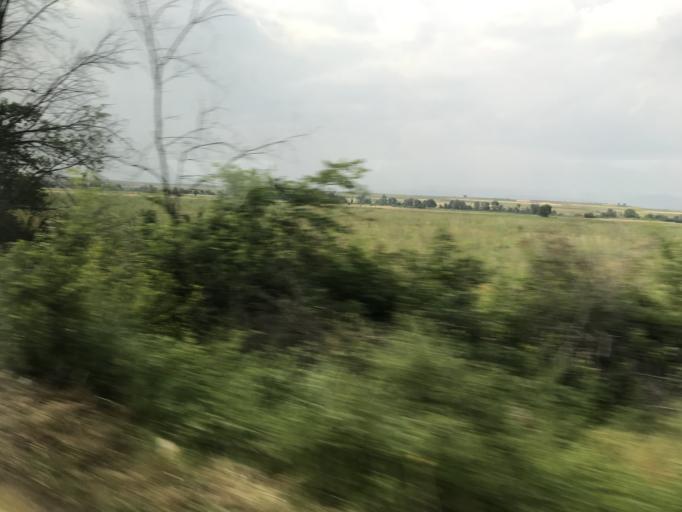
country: GR
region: East Macedonia and Thrace
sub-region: Nomos Rodopis
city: Lykeio
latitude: 41.0425
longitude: 25.6513
